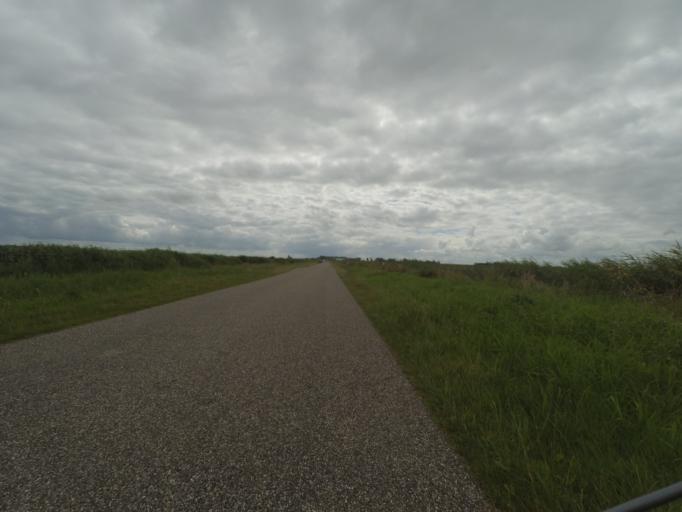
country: NL
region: Friesland
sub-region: Gemeente Dongeradeel
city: Anjum
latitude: 53.3474
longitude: 6.1530
